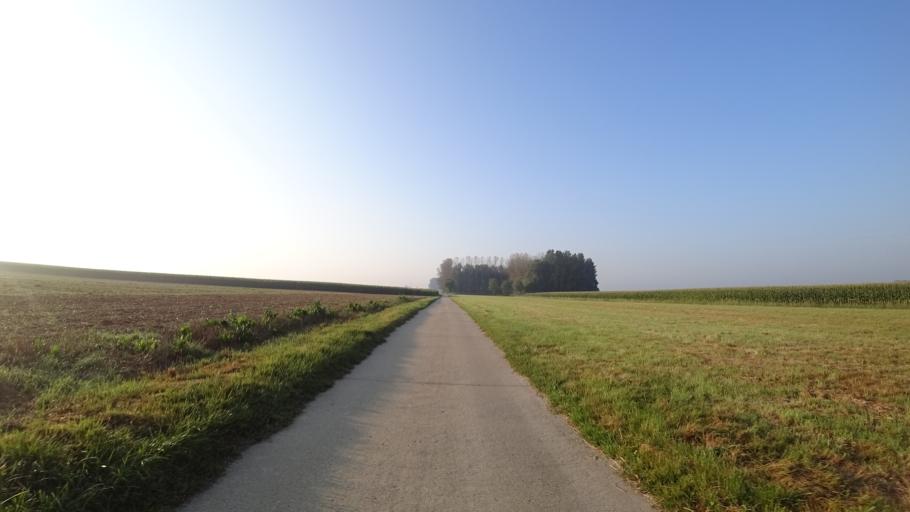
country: BE
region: Wallonia
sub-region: Province du Brabant Wallon
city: Walhain-Saint-Paul
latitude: 50.6284
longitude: 4.6758
